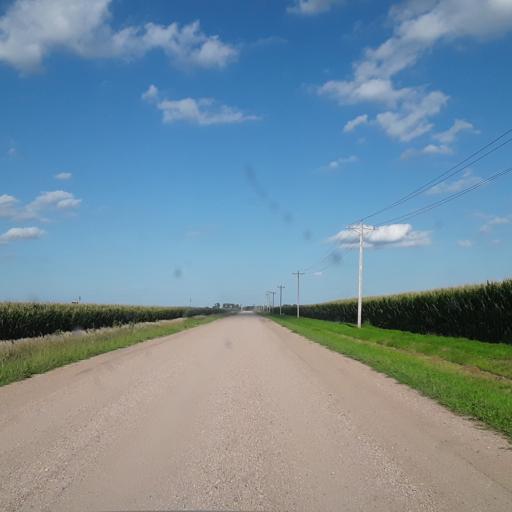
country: US
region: Nebraska
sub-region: Hall County
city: Wood River
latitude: 40.9167
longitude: -98.5839
